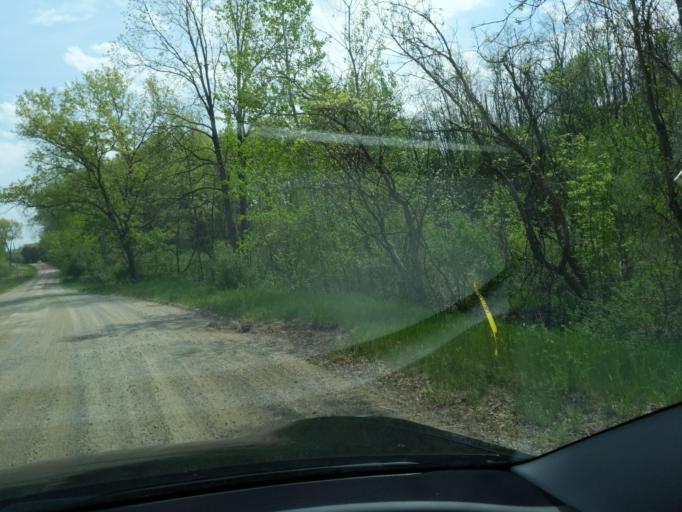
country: US
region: Michigan
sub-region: Ingham County
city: Stockbridge
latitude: 42.4352
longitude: -84.0762
